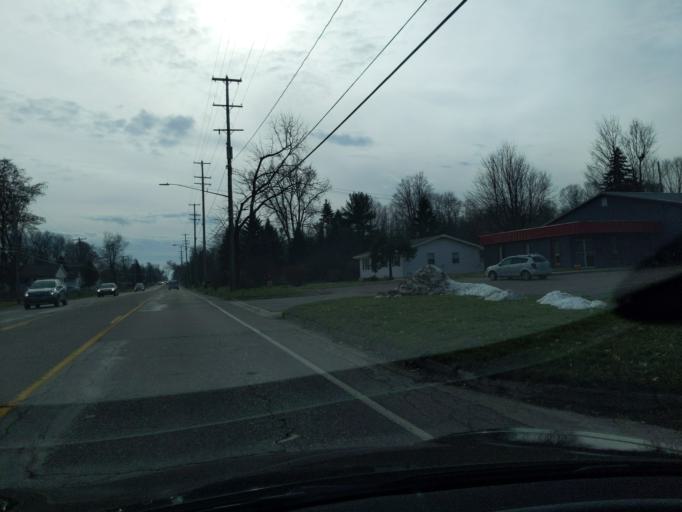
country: US
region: Michigan
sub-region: Ingham County
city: Holt
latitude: 42.6579
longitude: -84.5235
